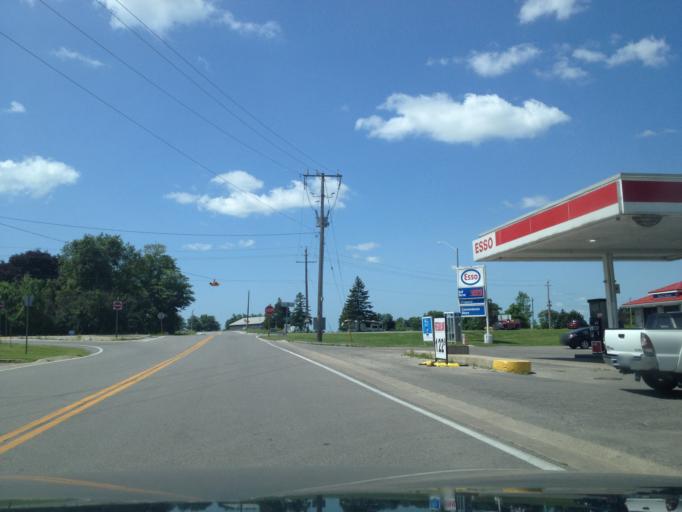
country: CA
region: Ontario
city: Norfolk County
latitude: 42.6131
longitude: -80.4624
